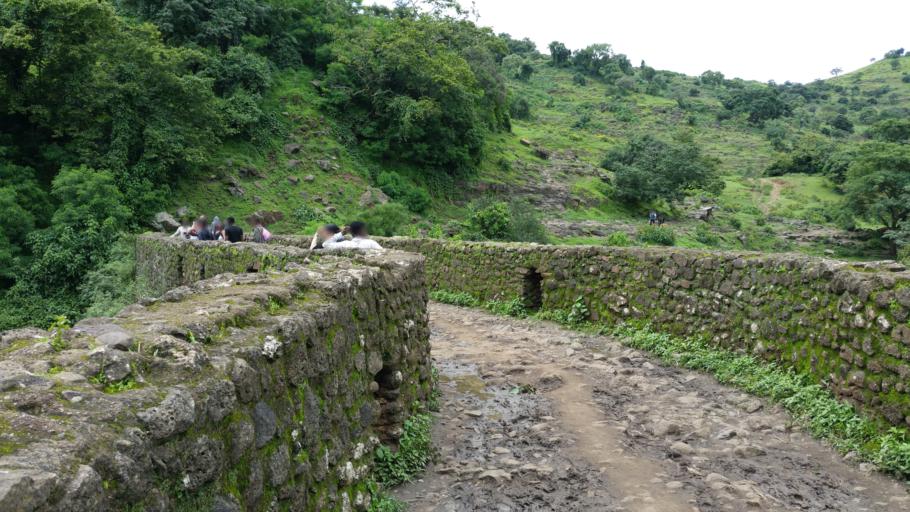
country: ET
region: Amhara
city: Bahir Dar
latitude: 11.4873
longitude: 37.5945
